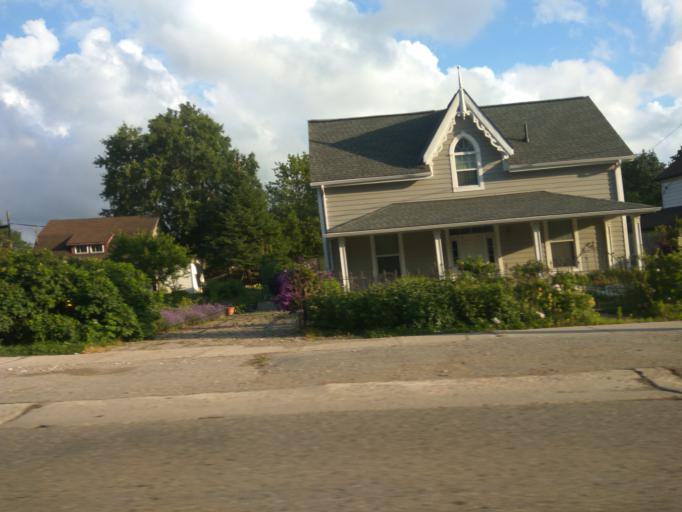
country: CA
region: Ontario
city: Stratford
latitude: 43.3696
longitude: -80.8389
